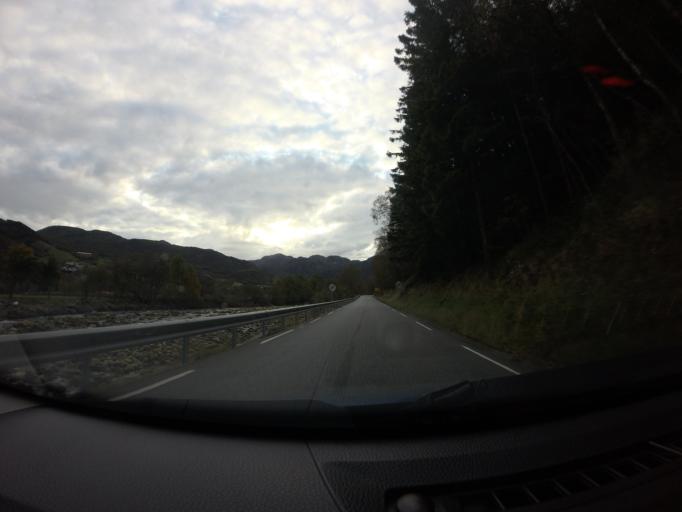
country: NO
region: Rogaland
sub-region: Forsand
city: Forsand
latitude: 58.8051
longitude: 6.2538
